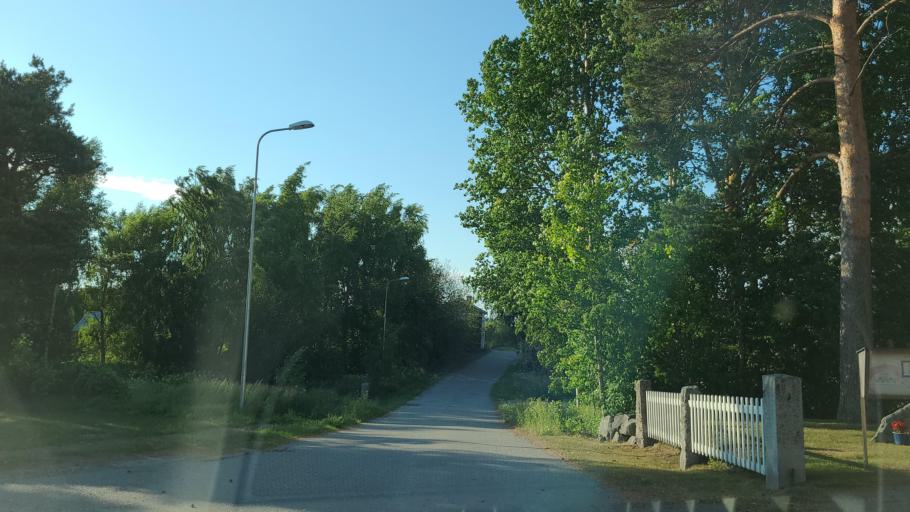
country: FI
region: Ostrobothnia
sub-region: Vaasa
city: Replot
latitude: 63.3467
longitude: 21.3331
